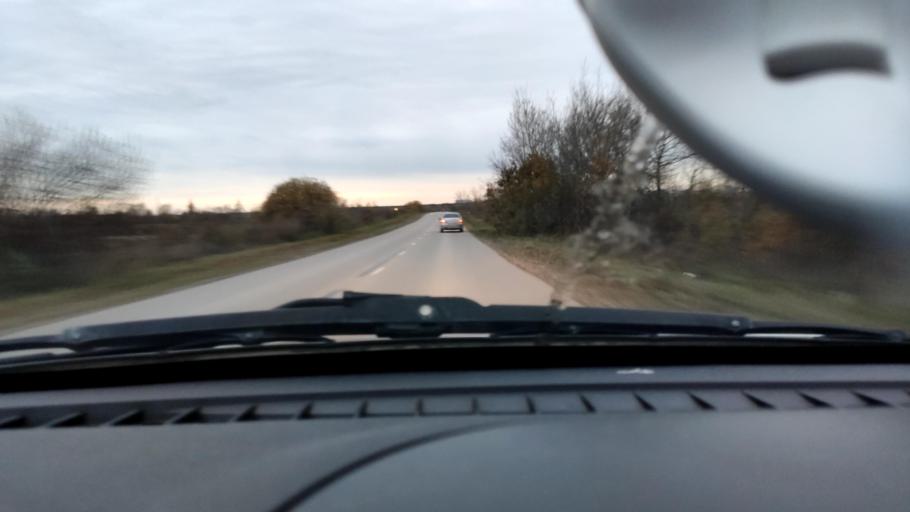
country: RU
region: Perm
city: Kondratovo
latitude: 58.0013
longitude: 56.0689
